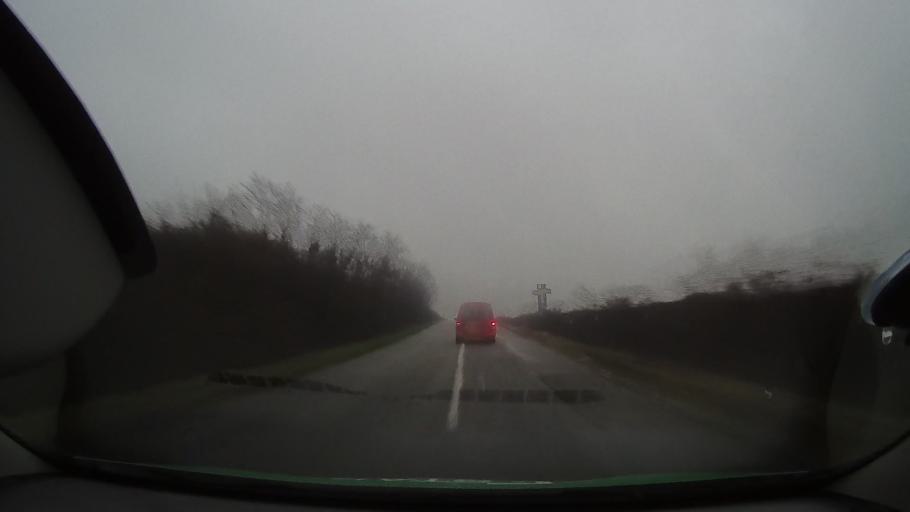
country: RO
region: Arad
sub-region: Comuna Craiova
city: Craiova
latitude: 46.6161
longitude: 21.9573
